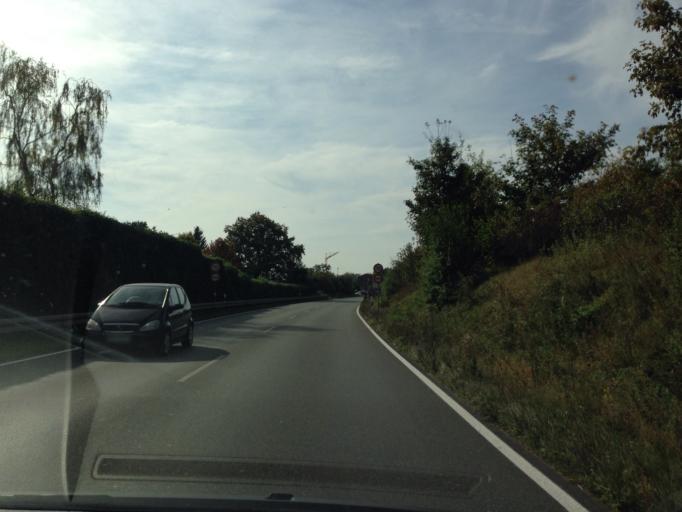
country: DE
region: North Rhine-Westphalia
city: Ludinghausen
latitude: 51.7679
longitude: 7.4640
